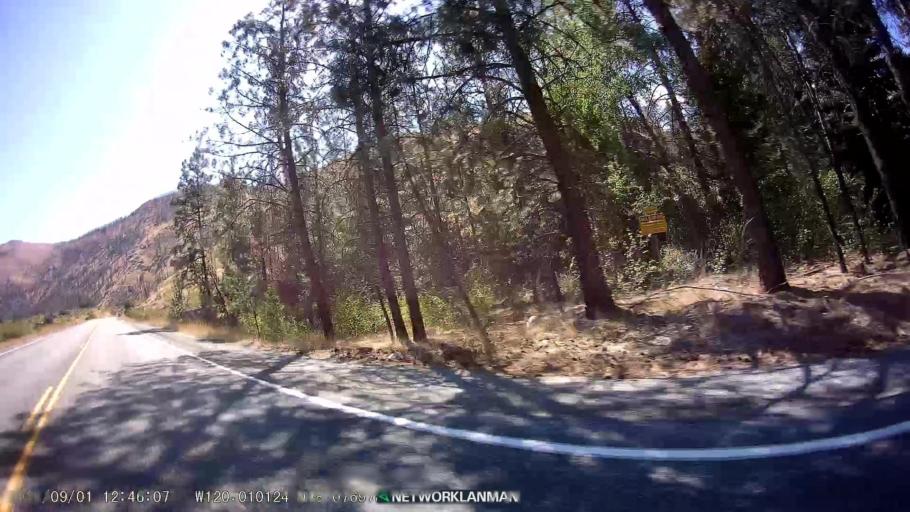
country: US
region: Washington
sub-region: Okanogan County
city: Brewster
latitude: 48.0758
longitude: -120.0103
